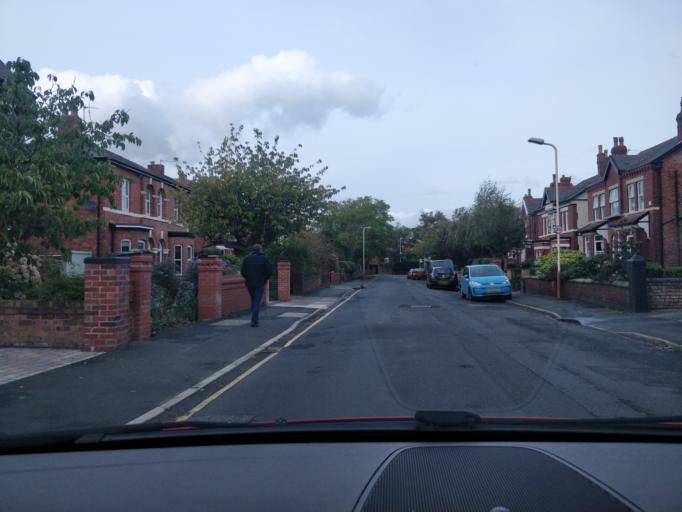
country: GB
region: England
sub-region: Sefton
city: Southport
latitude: 53.6280
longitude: -3.0170
